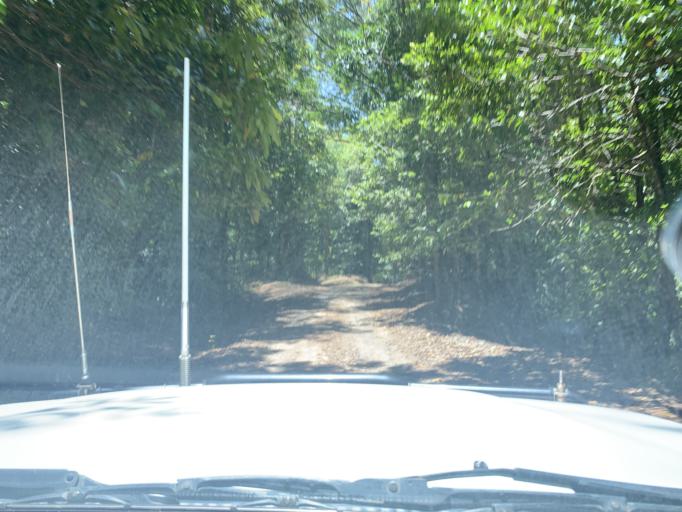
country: AU
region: Queensland
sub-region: Cairns
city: Redlynch
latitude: -16.9616
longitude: 145.6462
